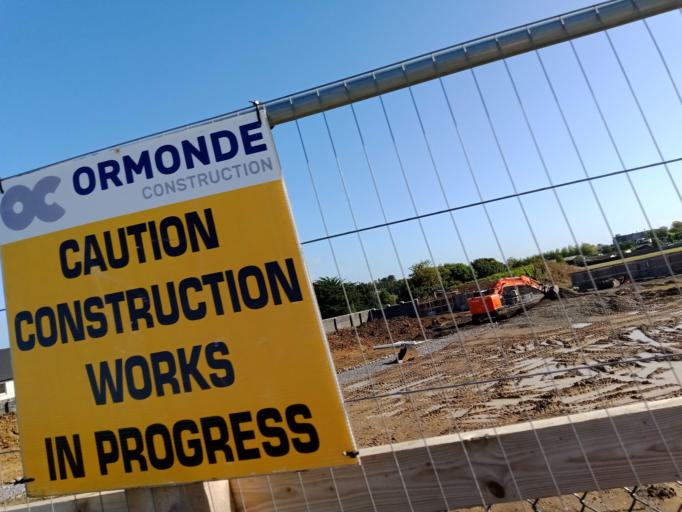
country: IE
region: Leinster
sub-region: Kilkenny
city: Kilkenny
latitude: 52.6447
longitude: -7.2688
